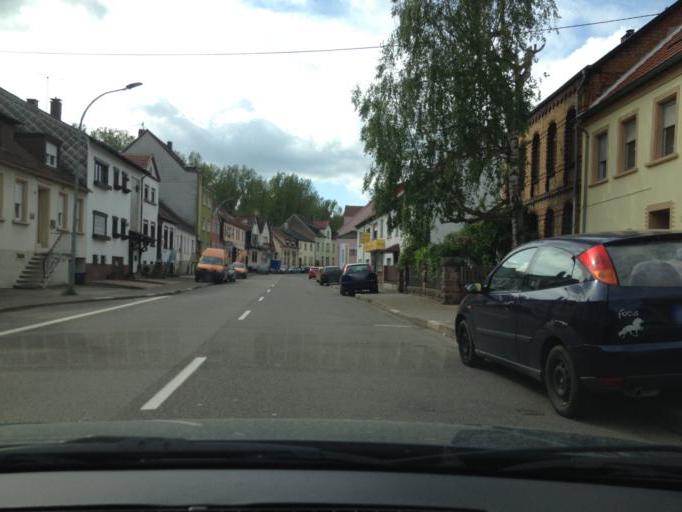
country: DE
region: Saarland
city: Hangard
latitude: 49.3749
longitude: 7.1850
